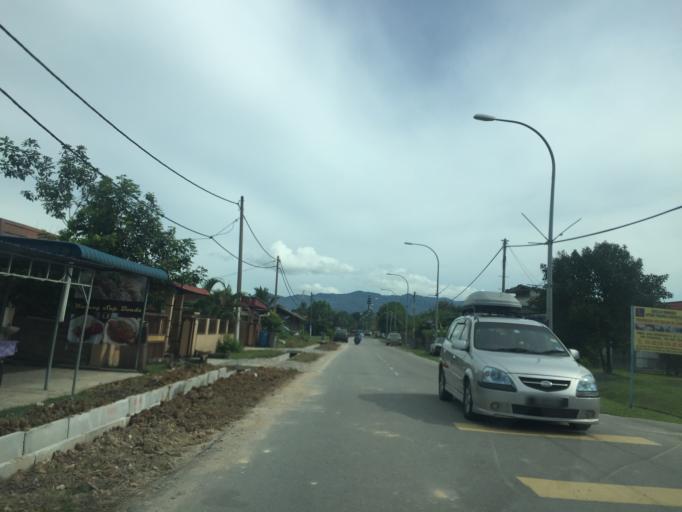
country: MY
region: Negeri Sembilan
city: Seremban
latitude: 2.7303
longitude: 101.9665
